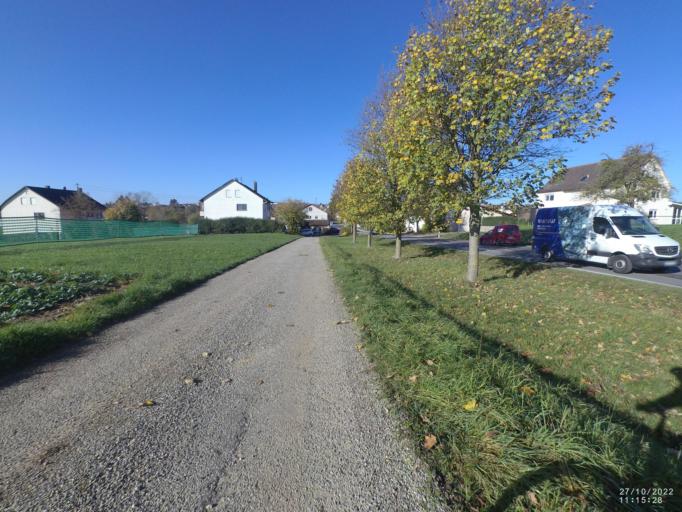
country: DE
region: Baden-Wuerttemberg
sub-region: Regierungsbezirk Stuttgart
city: Bohmenkirch
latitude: 48.6849
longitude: 9.9433
